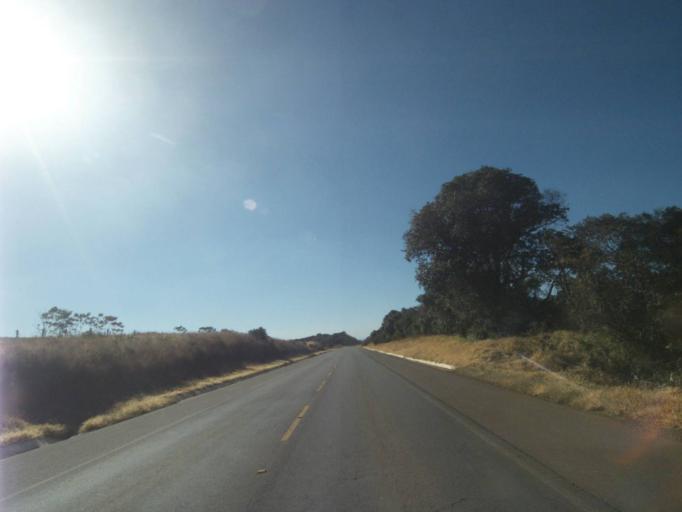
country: BR
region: Parana
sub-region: Tibagi
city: Tibagi
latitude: -24.7303
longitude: -50.4526
